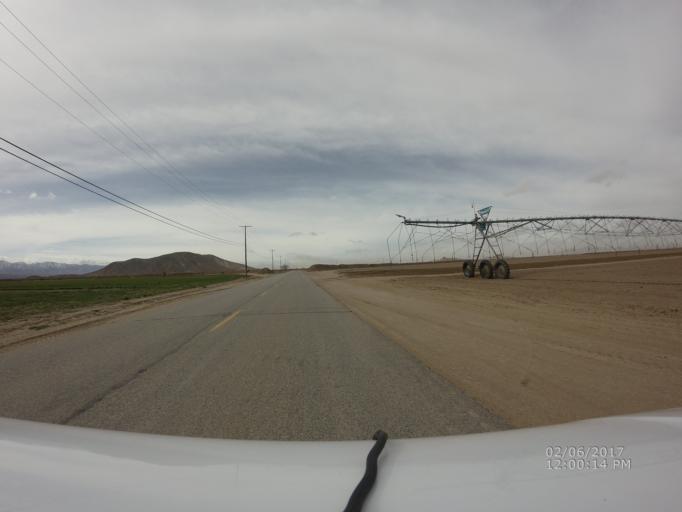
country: US
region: California
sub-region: Los Angeles County
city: Lake Los Angeles
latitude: 34.5652
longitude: -117.6979
